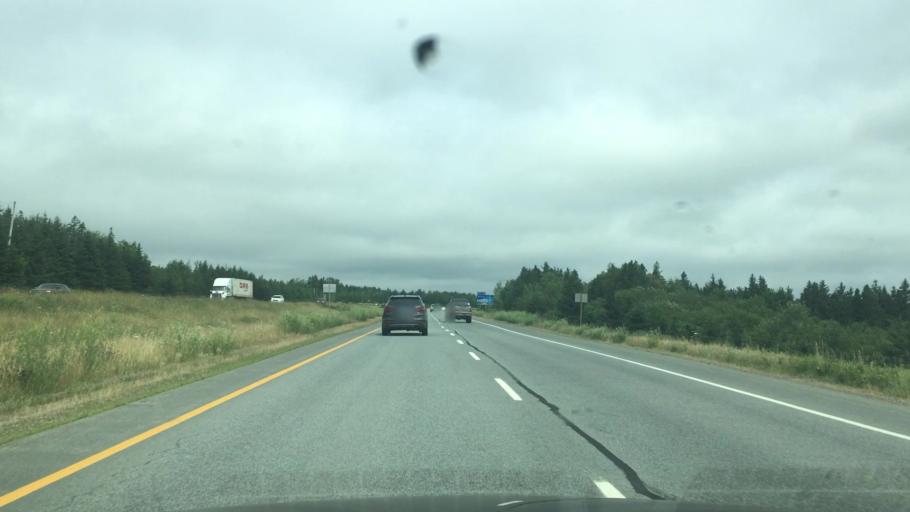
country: CA
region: Nova Scotia
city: Truro
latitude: 45.2980
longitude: -63.3026
